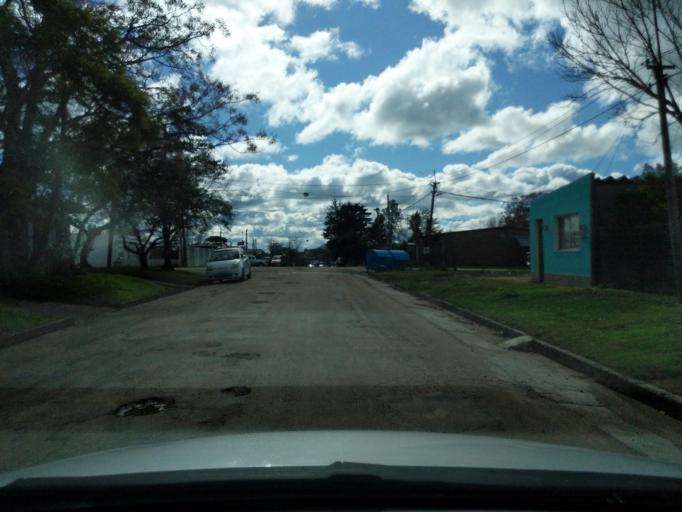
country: UY
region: Florida
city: Florida
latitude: -34.0948
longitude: -56.2302
